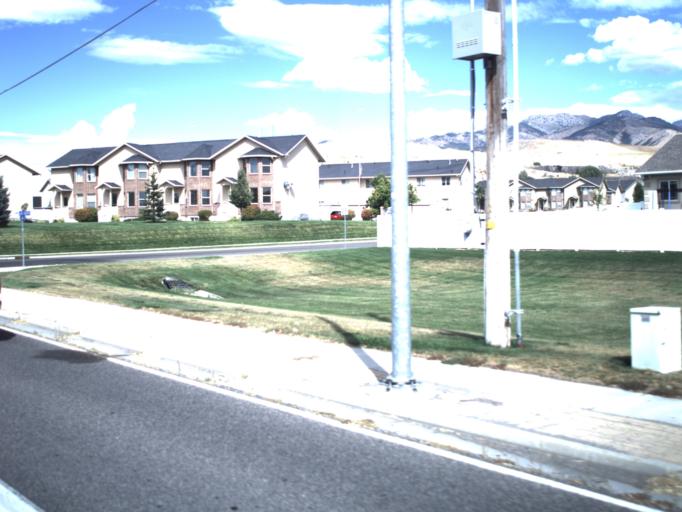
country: US
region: Utah
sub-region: Cache County
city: Smithfield
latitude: 41.8494
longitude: -111.8321
